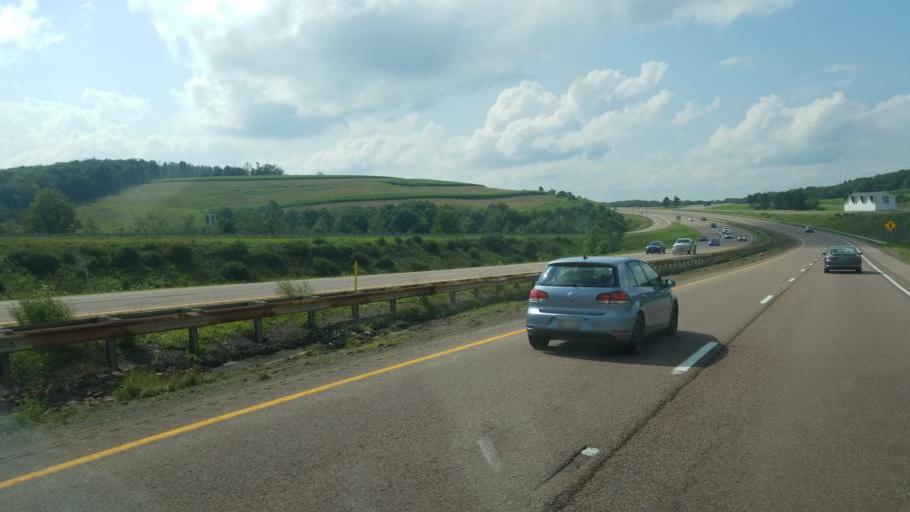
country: US
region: Maryland
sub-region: Allegany County
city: Frostburg
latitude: 39.6845
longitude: -78.9710
